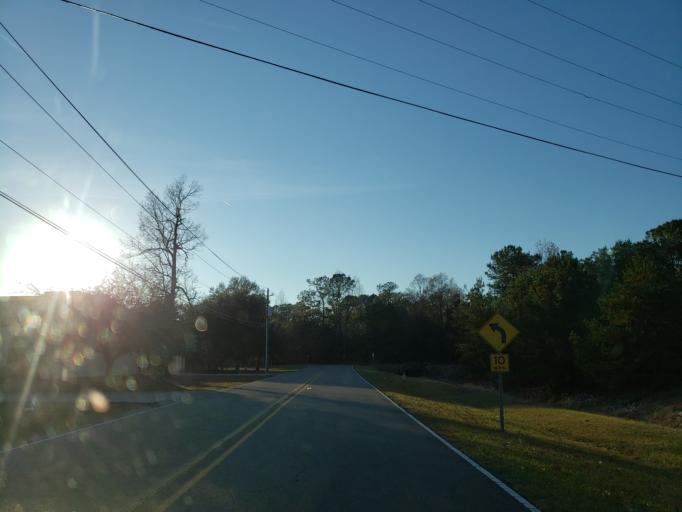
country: US
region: Mississippi
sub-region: Lamar County
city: Arnold Line
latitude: 31.3505
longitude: -89.3495
